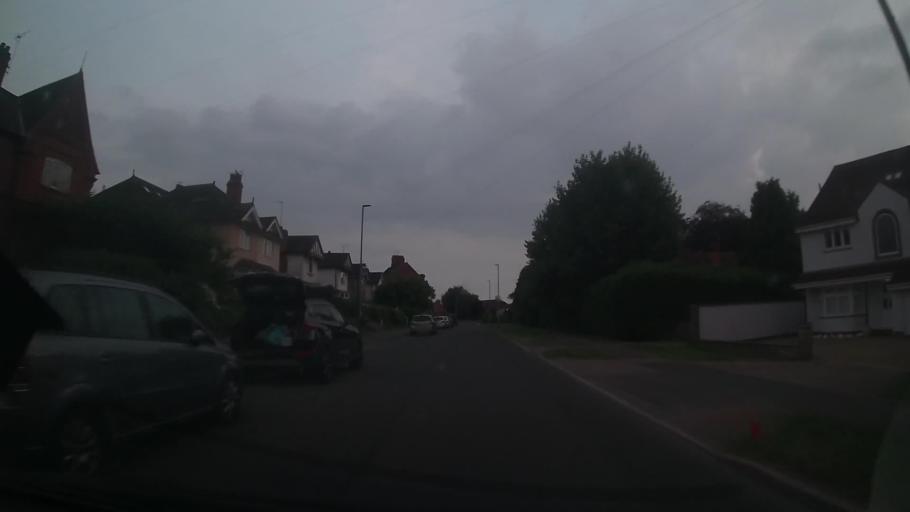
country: GB
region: England
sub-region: Leicestershire
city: Sileby
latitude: 52.7273
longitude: -1.1106
